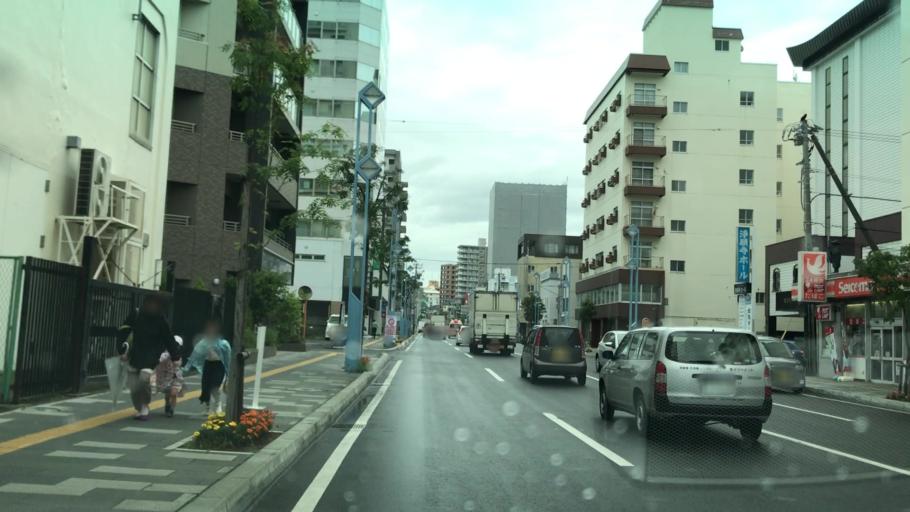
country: JP
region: Hokkaido
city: Sapporo
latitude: 43.0384
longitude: 141.3597
